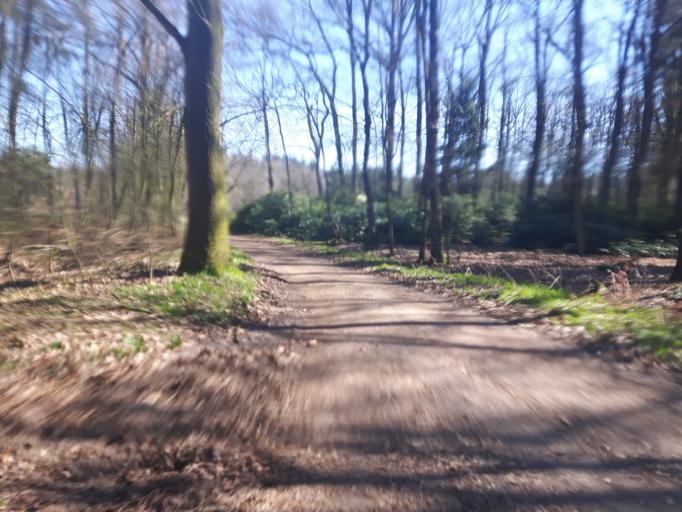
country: NL
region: Overijssel
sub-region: Gemeente Haaksbergen
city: Haaksbergen
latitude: 52.1631
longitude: 6.8222
